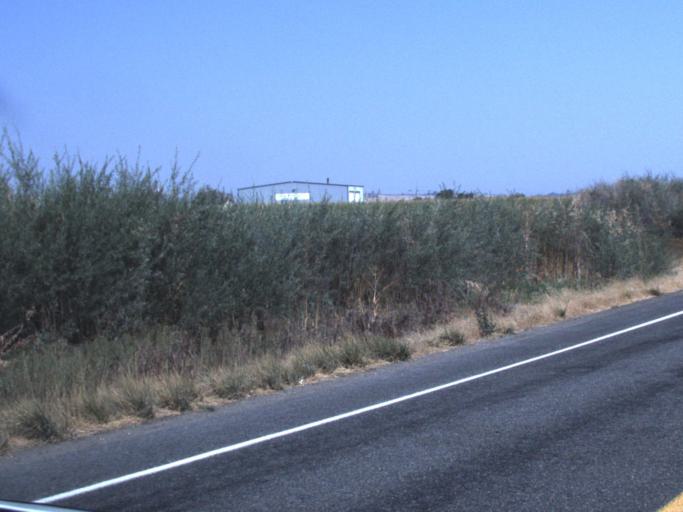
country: US
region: Washington
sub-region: Yakima County
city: Granger
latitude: 46.3262
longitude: -120.2428
